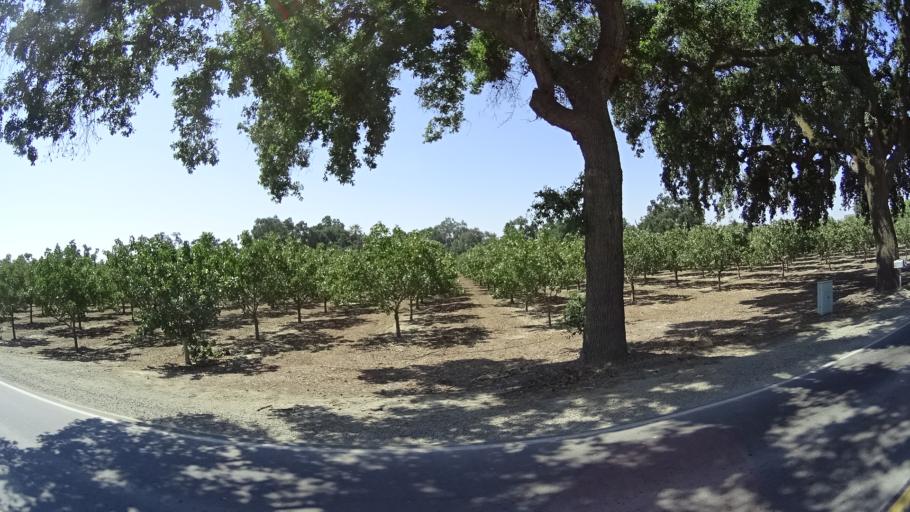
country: US
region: California
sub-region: Kings County
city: Lucerne
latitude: 36.3719
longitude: -119.6452
